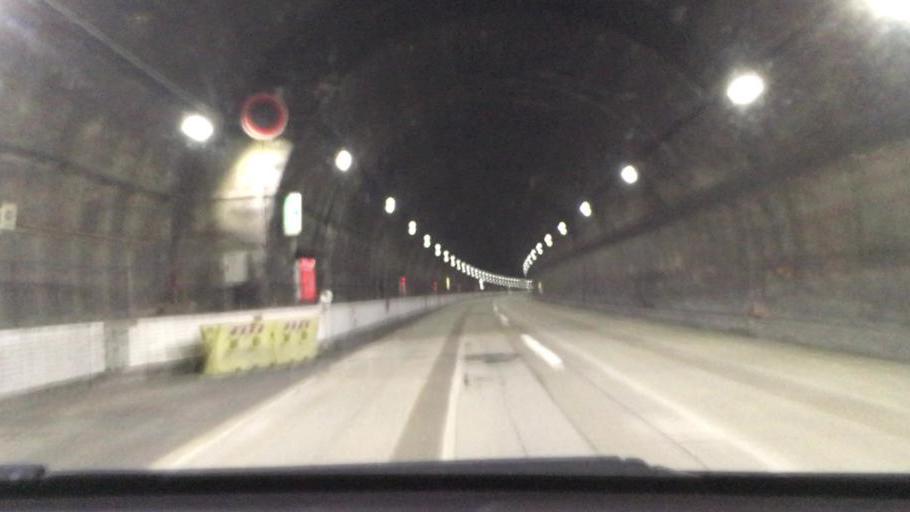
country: JP
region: Yamaguchi
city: Hofu
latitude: 34.0553
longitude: 131.6261
